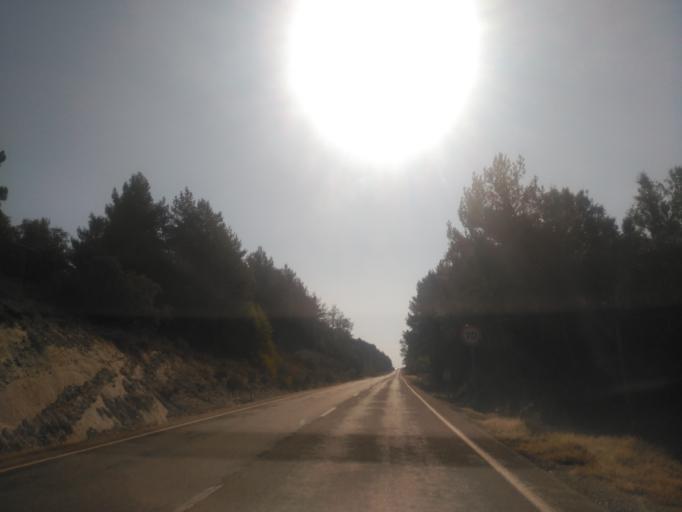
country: ES
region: Castille and Leon
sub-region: Provincia de Soria
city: San Leonardo de Yague
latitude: 41.8103
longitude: -3.0586
